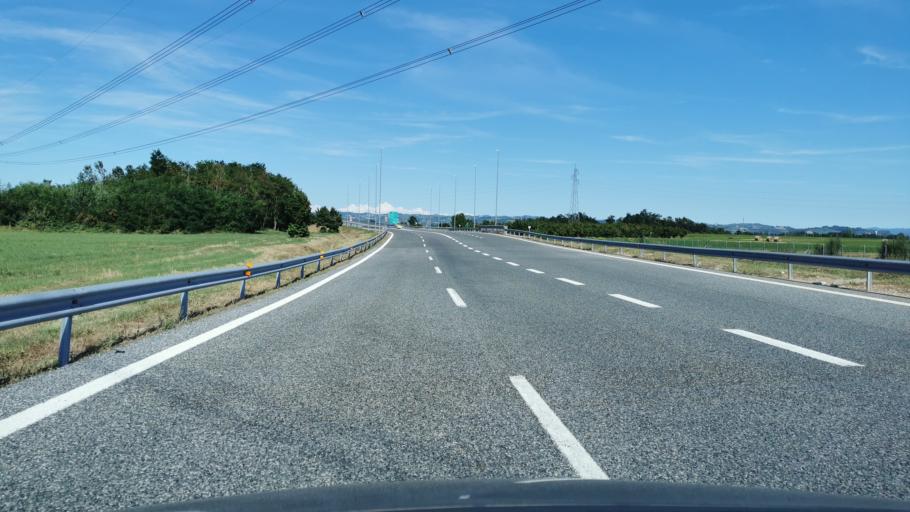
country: IT
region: Piedmont
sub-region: Provincia di Cuneo
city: Magliano Alpi
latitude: 44.4858
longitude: 7.8140
